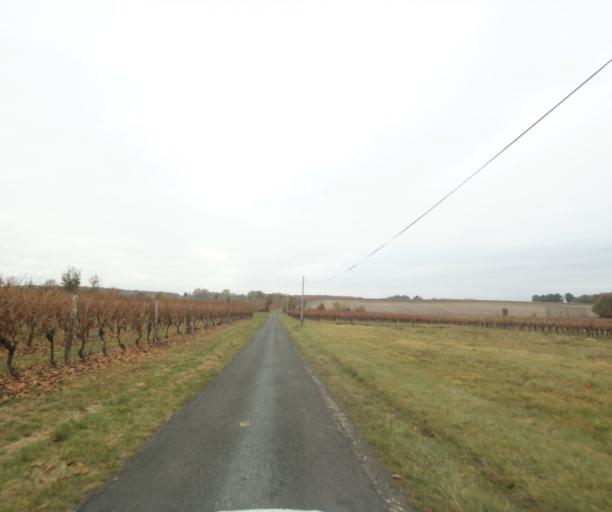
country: FR
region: Poitou-Charentes
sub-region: Departement de la Charente-Maritime
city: Chermignac
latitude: 45.7100
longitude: -0.6821
